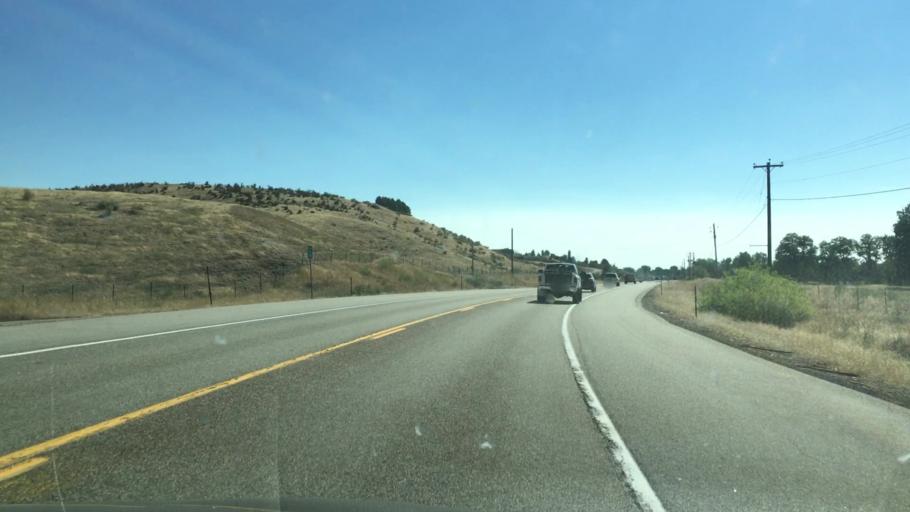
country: US
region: Idaho
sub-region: Ada County
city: Eagle
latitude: 43.7287
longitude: -116.3059
